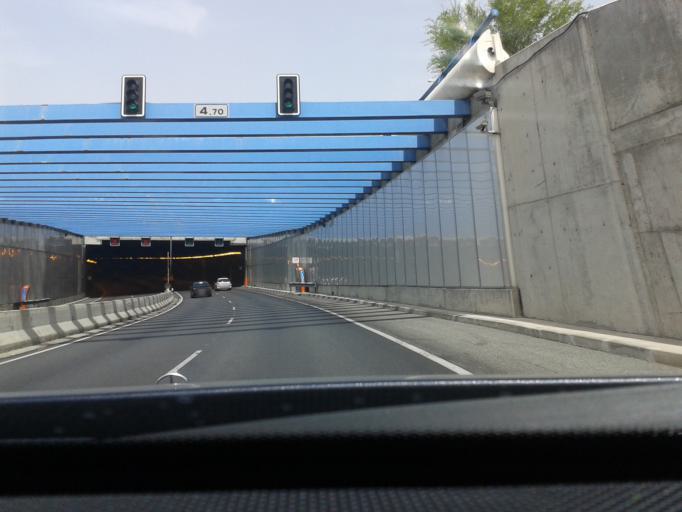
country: ES
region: Madrid
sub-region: Provincia de Madrid
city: Barajas de Madrid
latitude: 40.4746
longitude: -3.5742
